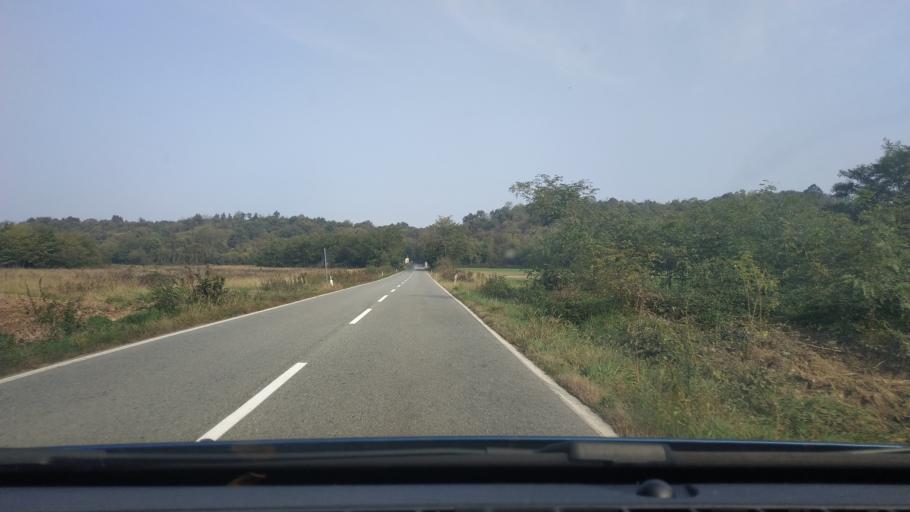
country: IT
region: Piedmont
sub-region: Provincia di Torino
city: Montalenghe
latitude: 45.3440
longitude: 7.8372
